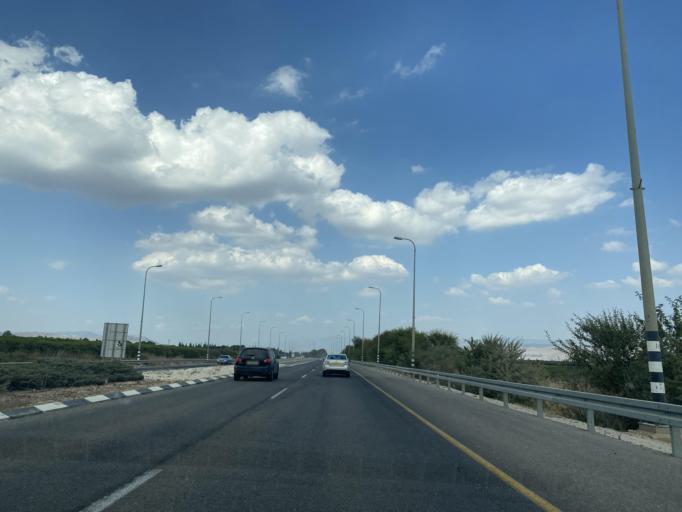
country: IL
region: Northern District
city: Rosh Pinna
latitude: 32.9933
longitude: 35.5627
